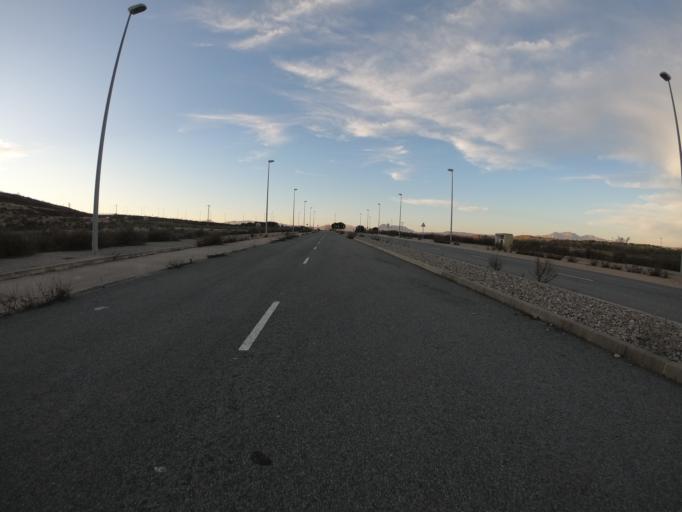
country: ES
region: Basque Country
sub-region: Provincia de Alava
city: Oyon
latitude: 42.4846
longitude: -2.4151
